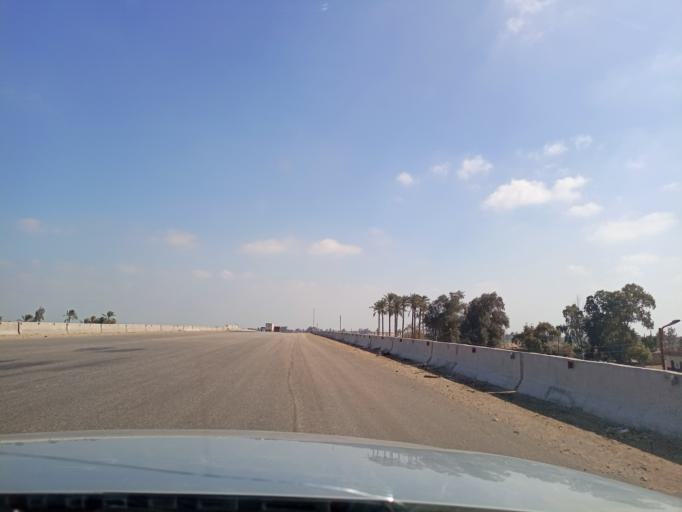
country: EG
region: Eastern Province
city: Mashtul as Suq
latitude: 30.4621
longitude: 31.3657
